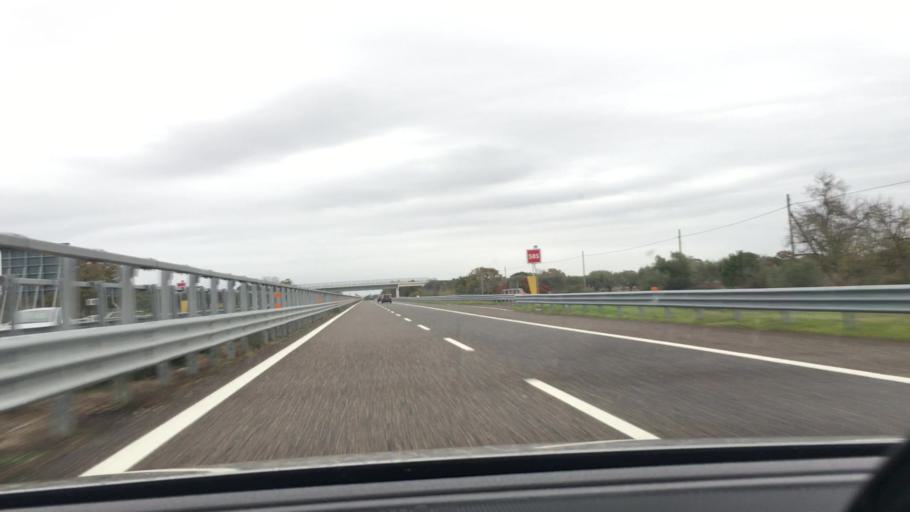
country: IT
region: Apulia
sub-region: Provincia di Bari
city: Gioia del Colle
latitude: 40.7463
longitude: 16.9148
